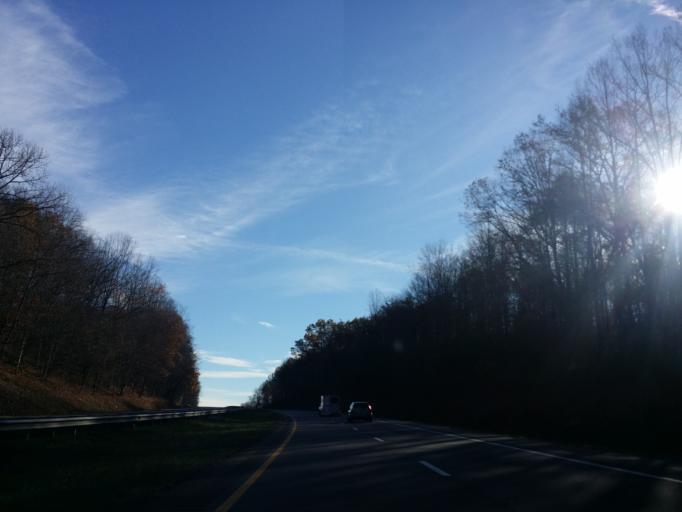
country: US
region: North Carolina
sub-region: McDowell County
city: West Marion
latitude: 35.6362
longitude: -82.1048
